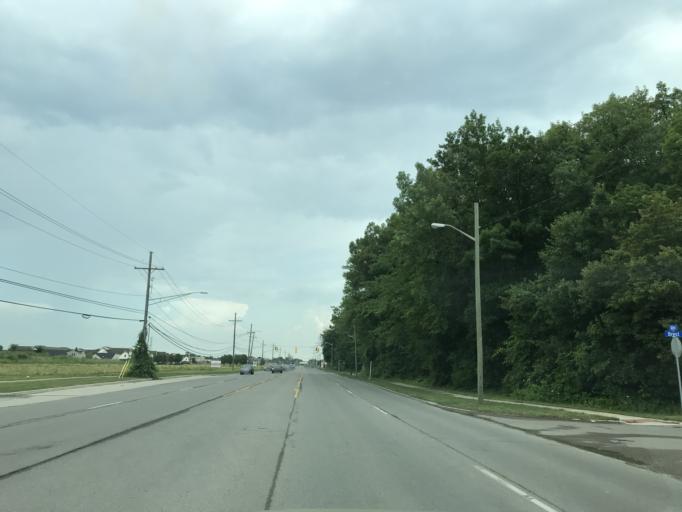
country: US
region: Michigan
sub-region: Wayne County
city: Southgate
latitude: 42.2205
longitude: -83.2296
